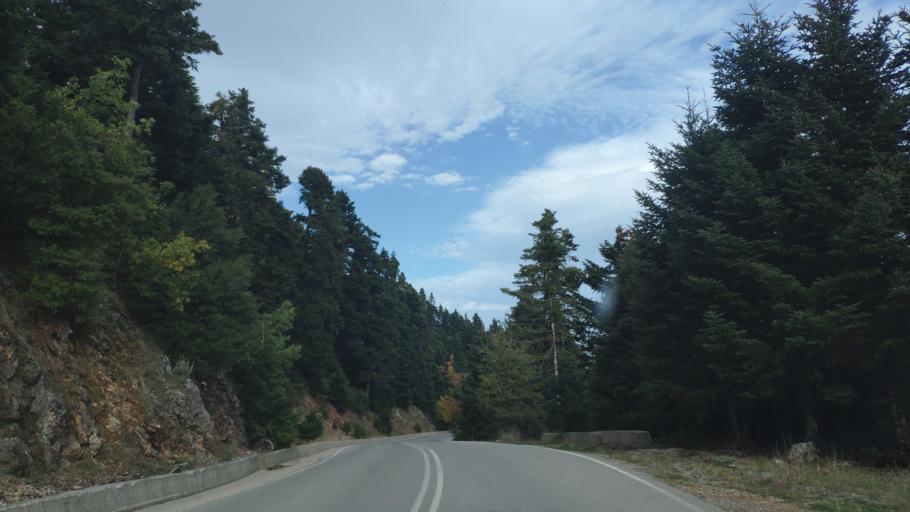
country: GR
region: Central Greece
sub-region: Nomos Fokidos
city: Amfissa
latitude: 38.6588
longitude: 22.3817
